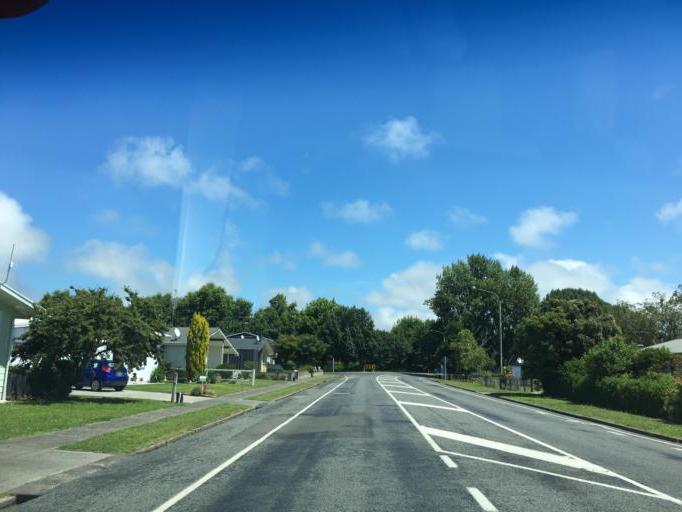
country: NZ
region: Hawke's Bay
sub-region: Wairoa District
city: Wairoa
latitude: -39.0372
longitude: 177.4155
